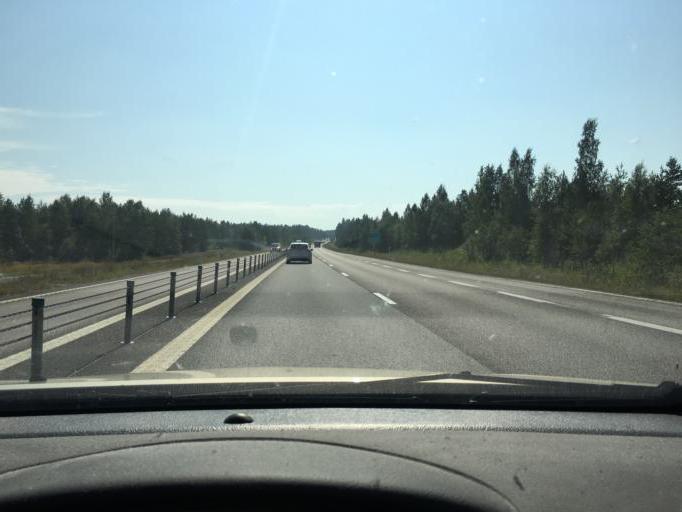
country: SE
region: Norrbotten
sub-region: Lulea Kommun
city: Gammelstad
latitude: 65.6116
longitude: 22.0555
